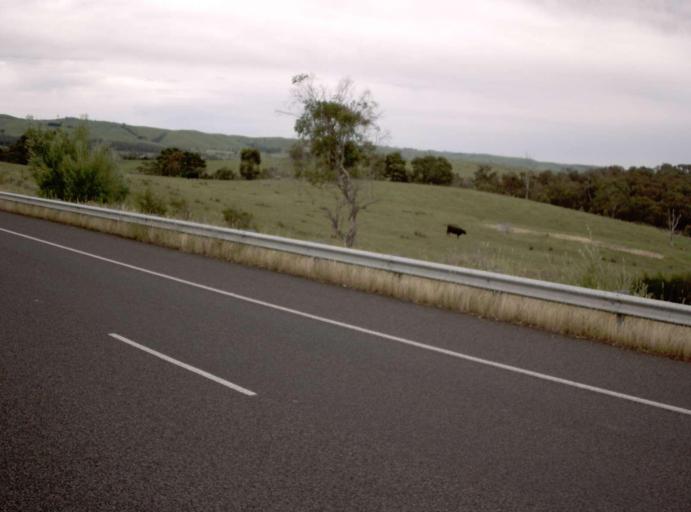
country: AU
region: Victoria
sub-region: Cardinia
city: Koo-Wee-Rup
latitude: -38.3584
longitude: 145.6533
